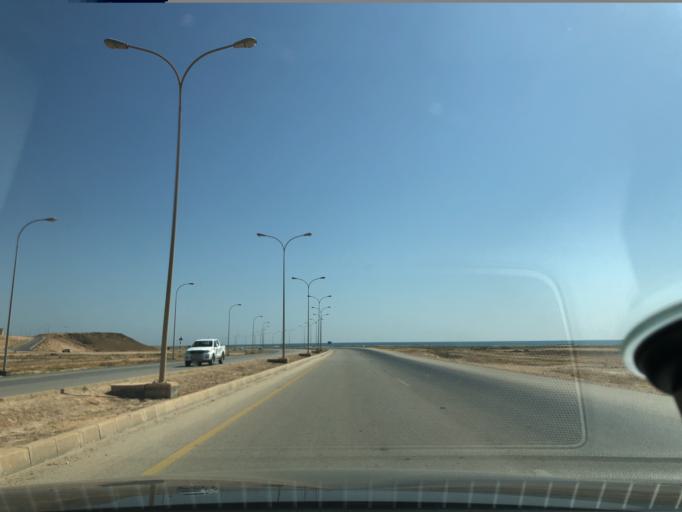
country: OM
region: Zufar
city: Salalah
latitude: 17.0396
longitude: 54.3411
